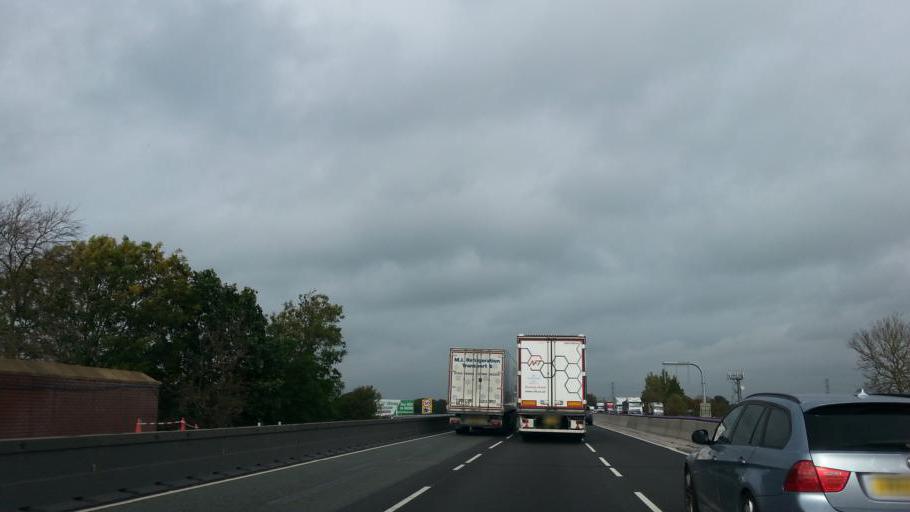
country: GB
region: England
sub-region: Cheshire East
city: Alsager
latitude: 53.0838
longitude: -2.3417
